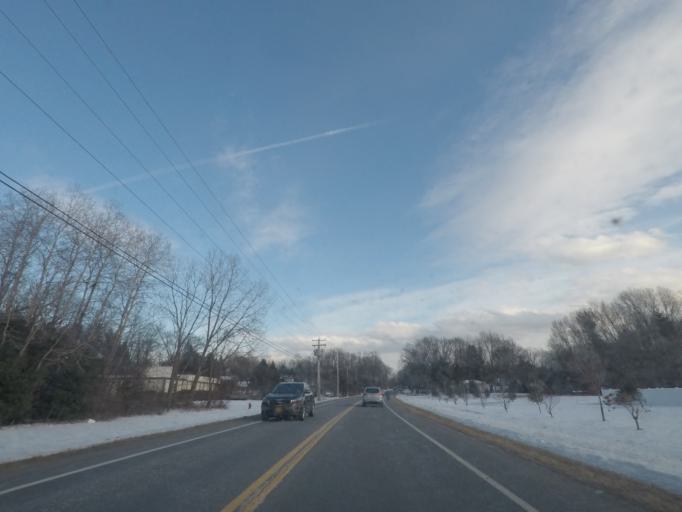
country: US
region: New York
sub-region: Saratoga County
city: Country Knolls
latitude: 42.8400
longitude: -73.7835
